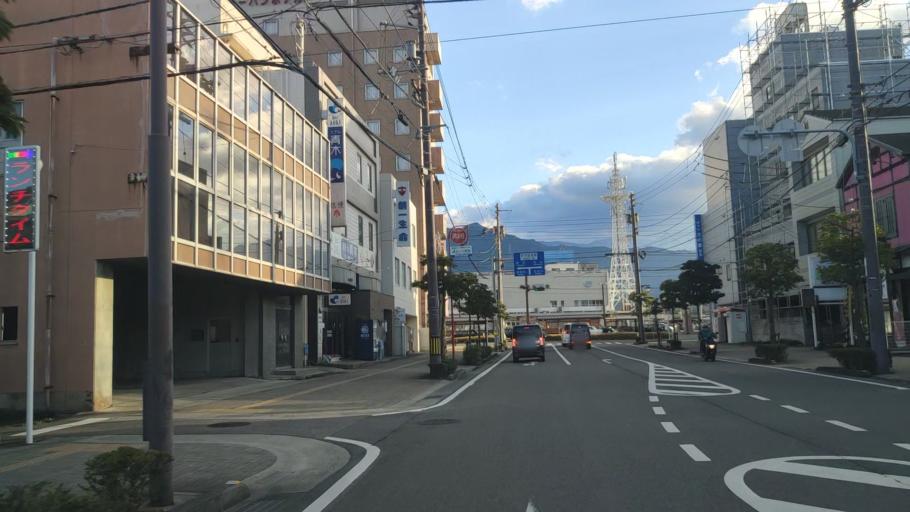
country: JP
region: Ehime
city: Saijo
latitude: 33.9137
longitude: 133.1871
